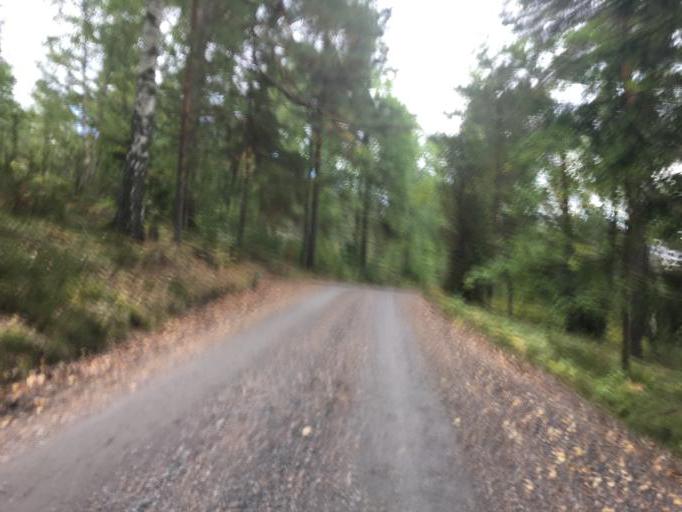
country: SE
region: Soedermanland
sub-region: Eskilstuna Kommun
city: Arla
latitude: 59.4548
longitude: 16.6811
